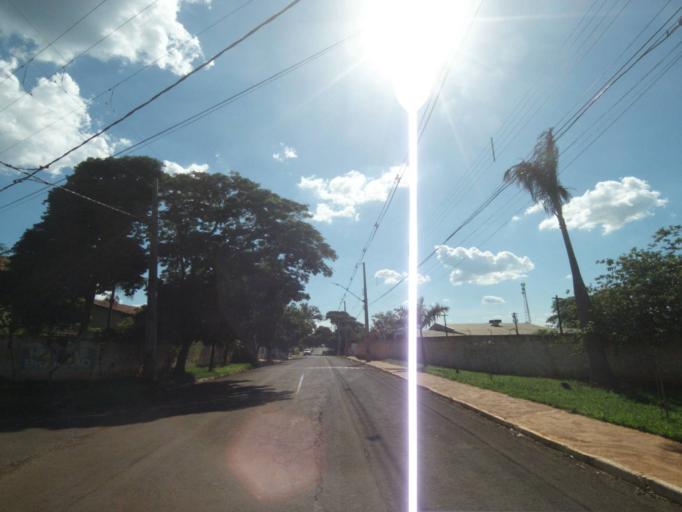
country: BR
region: Parana
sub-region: Sertanopolis
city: Sertanopolis
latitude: -23.0403
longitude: -50.8135
